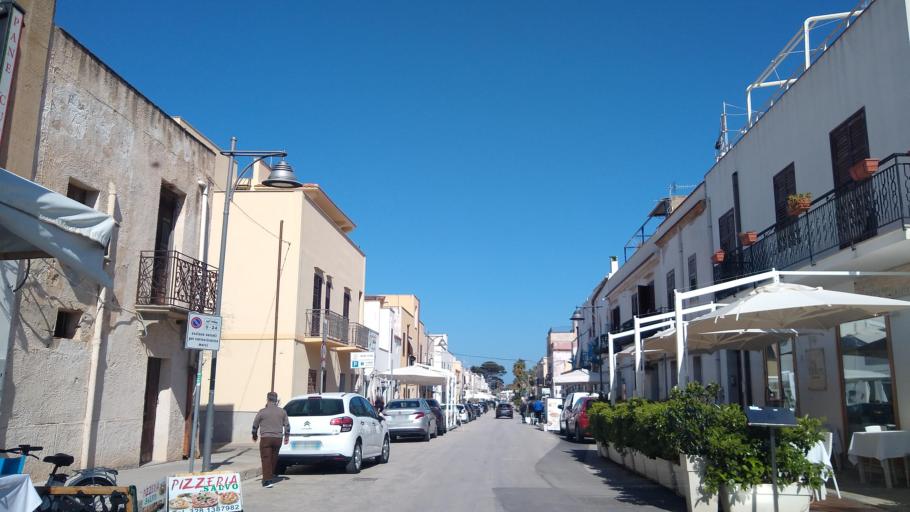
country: IT
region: Sicily
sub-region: Trapani
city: San Vito Lo Capo
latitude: 38.1751
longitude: 12.7341
